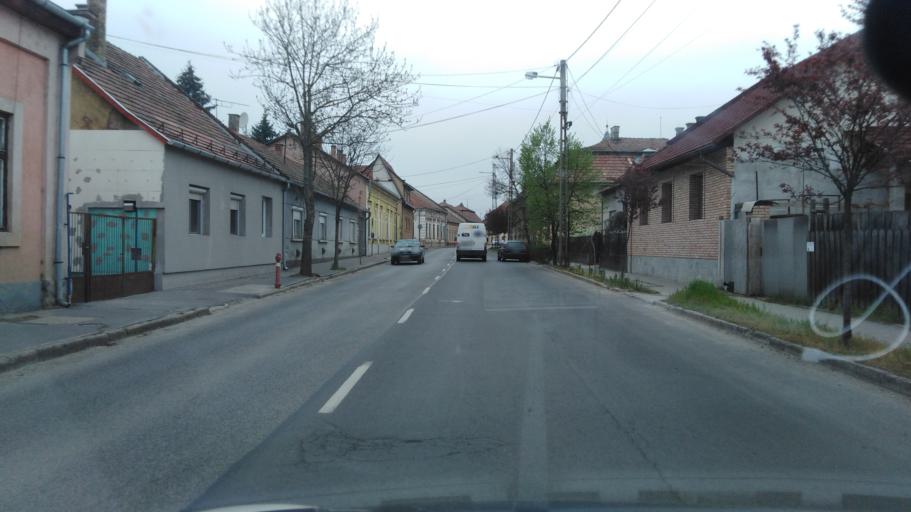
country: HU
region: Nograd
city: Balassagyarmat
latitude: 48.0750
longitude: 19.2962
